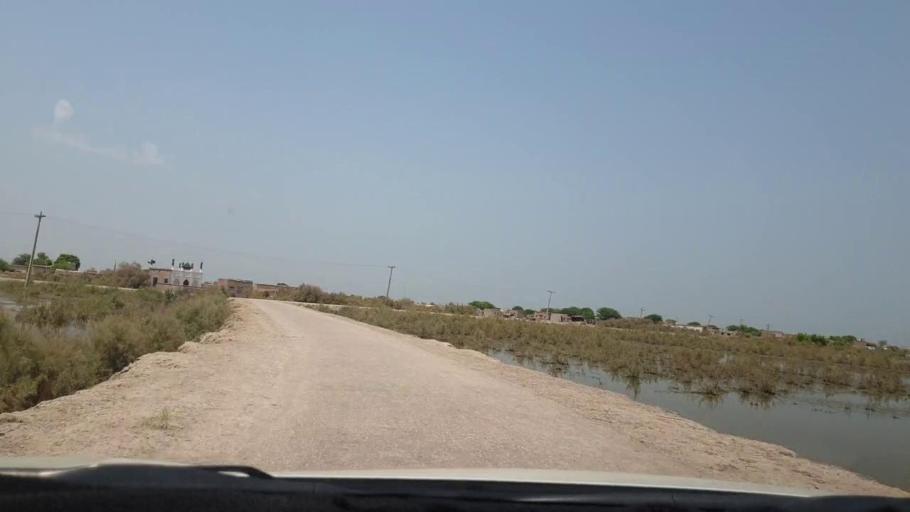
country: PK
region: Sindh
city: Radhan
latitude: 27.2472
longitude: 67.9936
